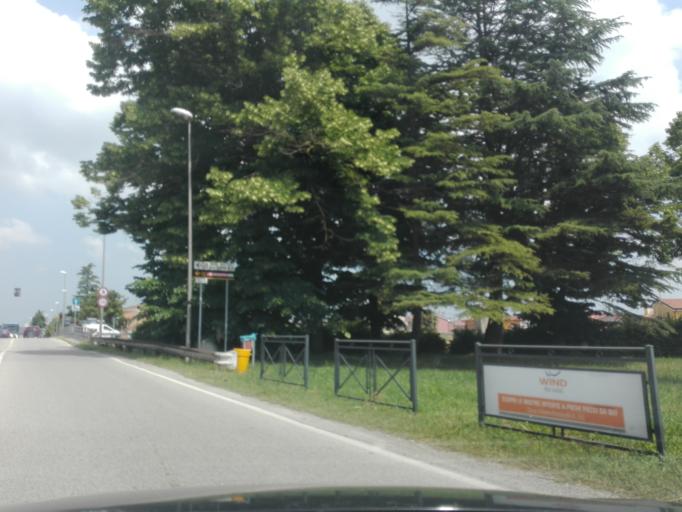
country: IT
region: Veneto
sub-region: Provincia di Rovigo
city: Adria
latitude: 45.0528
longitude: 12.0630
